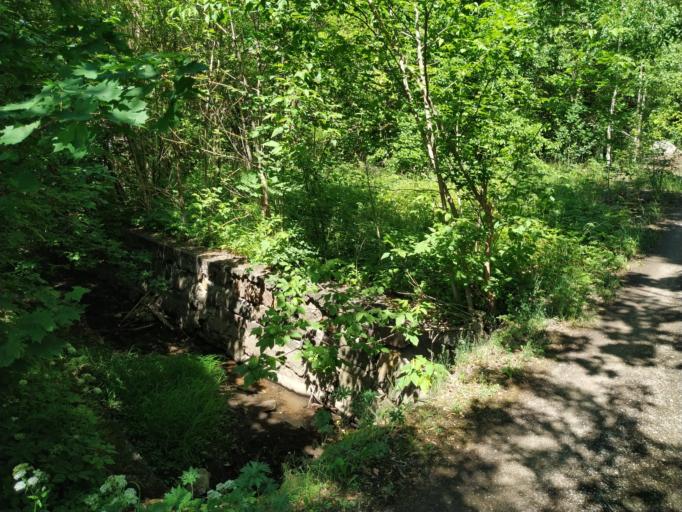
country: LT
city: Nemencine
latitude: 54.8723
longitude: 25.5407
